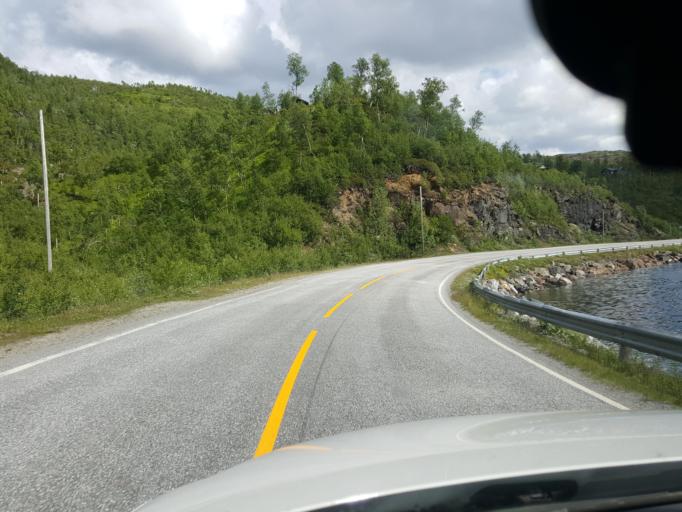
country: NO
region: Nordland
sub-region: Rana
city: Mo i Rana
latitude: 66.2858
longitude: 14.5273
